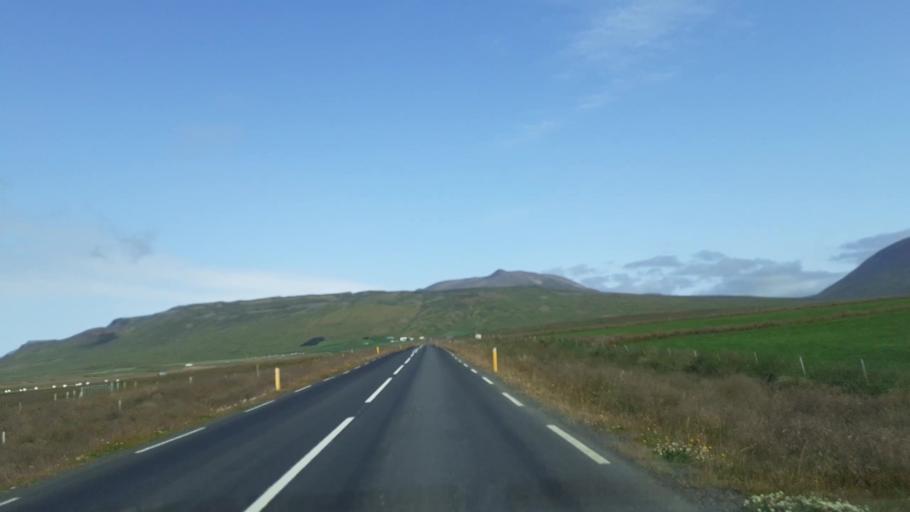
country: IS
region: Northwest
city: Saudarkrokur
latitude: 65.7122
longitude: -20.2269
